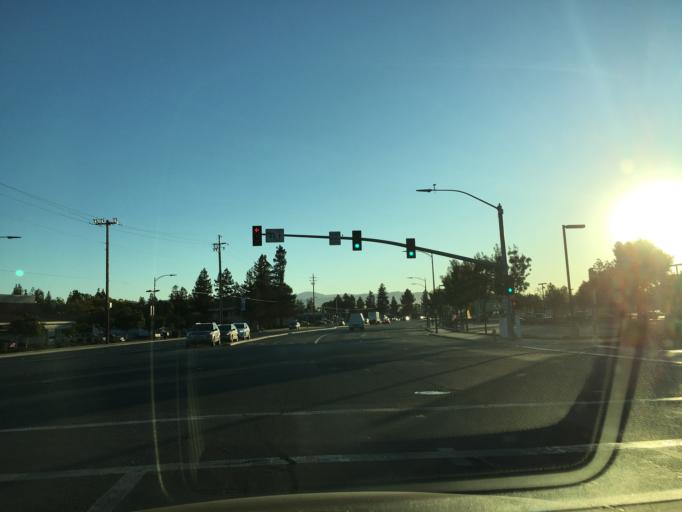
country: US
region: California
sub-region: Santa Clara County
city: Cambrian Park
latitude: 37.2503
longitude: -121.8780
